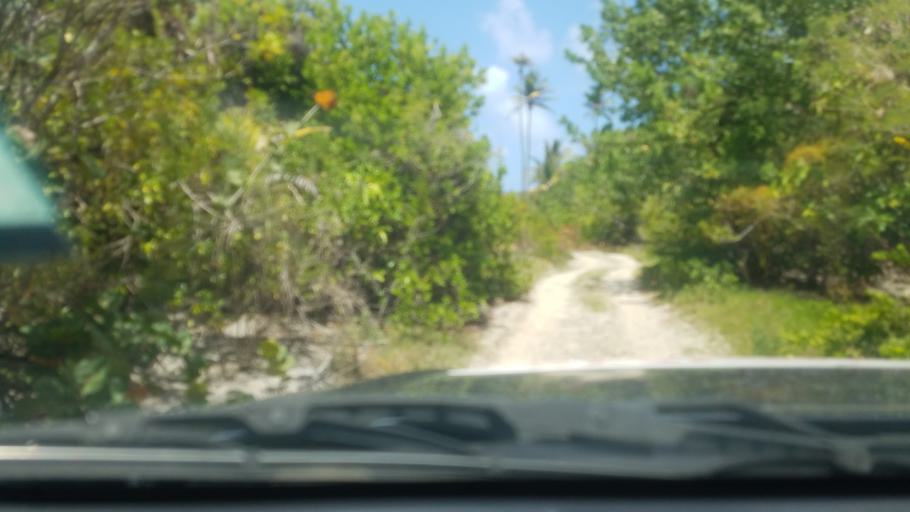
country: LC
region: Vieux-Fort
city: Vieux Fort
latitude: 13.7481
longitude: -60.9341
